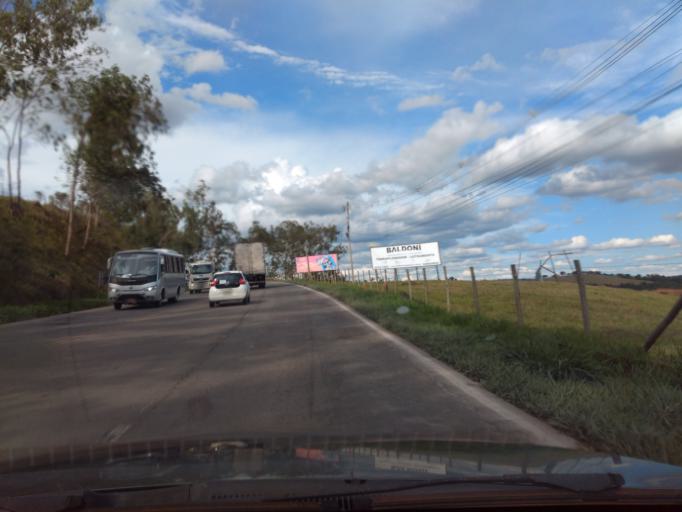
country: BR
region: Minas Gerais
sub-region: Varginha
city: Varginha
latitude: -21.6074
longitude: -45.4325
